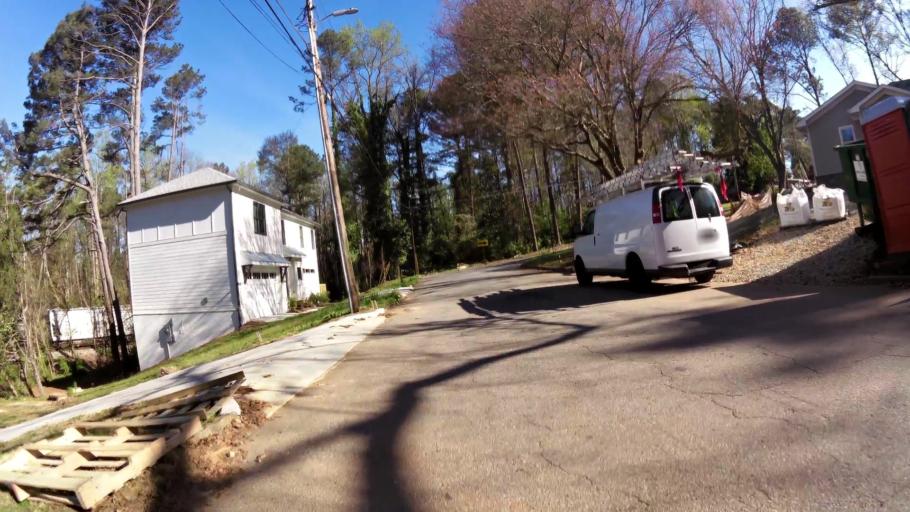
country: US
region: Georgia
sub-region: DeKalb County
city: Clarkston
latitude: 33.8327
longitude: -84.2651
